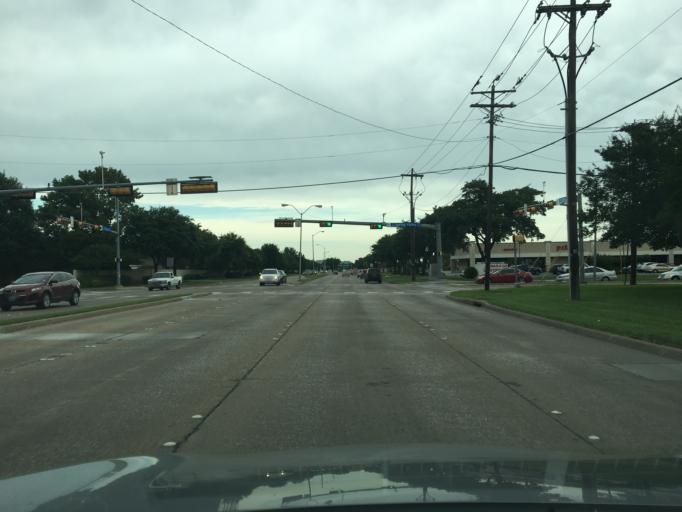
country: US
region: Texas
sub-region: Dallas County
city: Richardson
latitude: 32.9381
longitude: -96.6999
